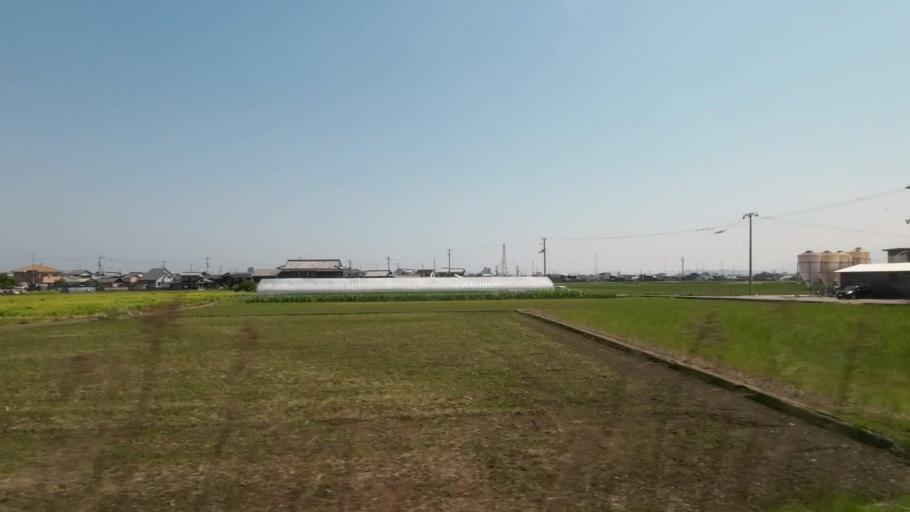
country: JP
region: Ehime
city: Saijo
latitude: 33.9228
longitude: 133.0917
